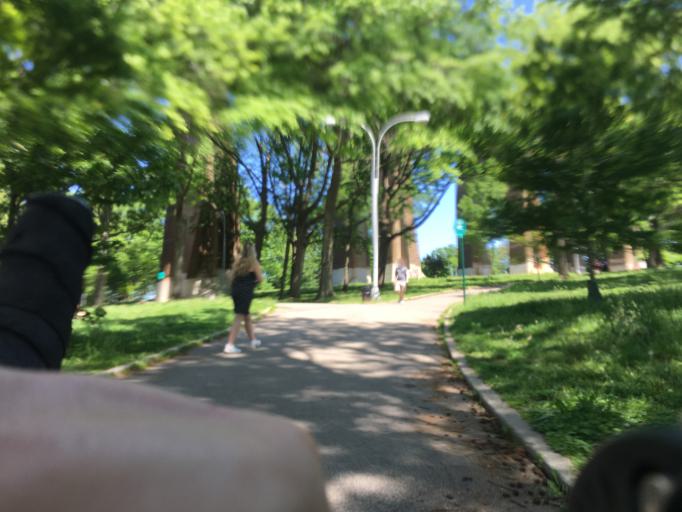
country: US
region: New York
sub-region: New York County
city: Manhattan
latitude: 40.7810
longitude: -73.9212
